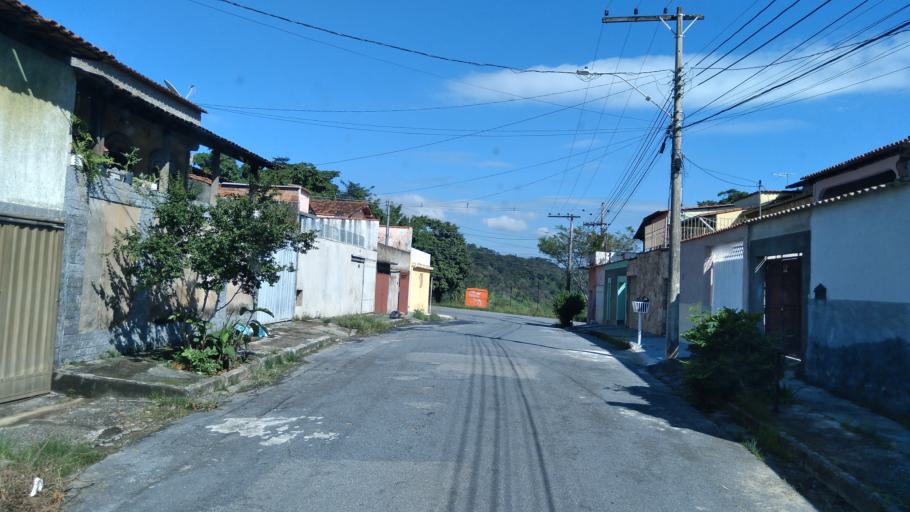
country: BR
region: Minas Gerais
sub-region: Santa Luzia
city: Santa Luzia
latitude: -19.8264
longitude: -43.9006
